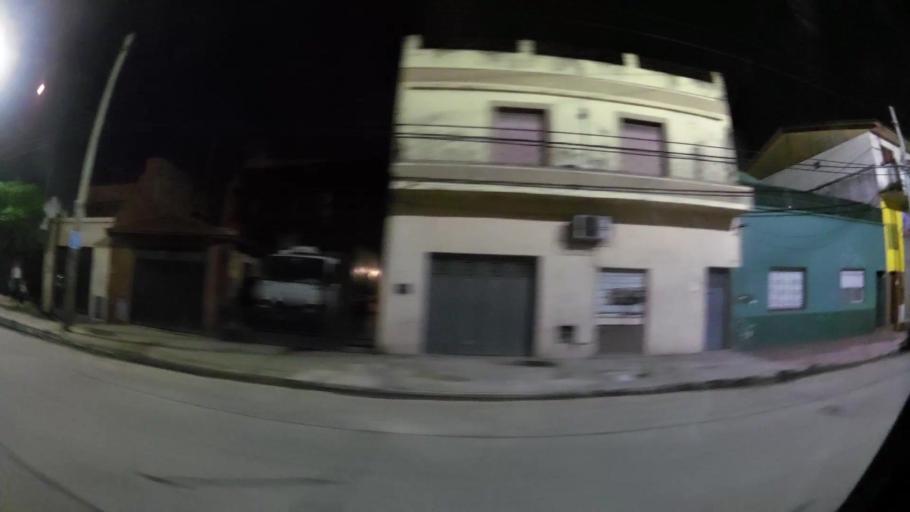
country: AR
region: Buenos Aires
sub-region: Partido de Lanus
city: Lanus
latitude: -34.7184
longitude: -58.3583
